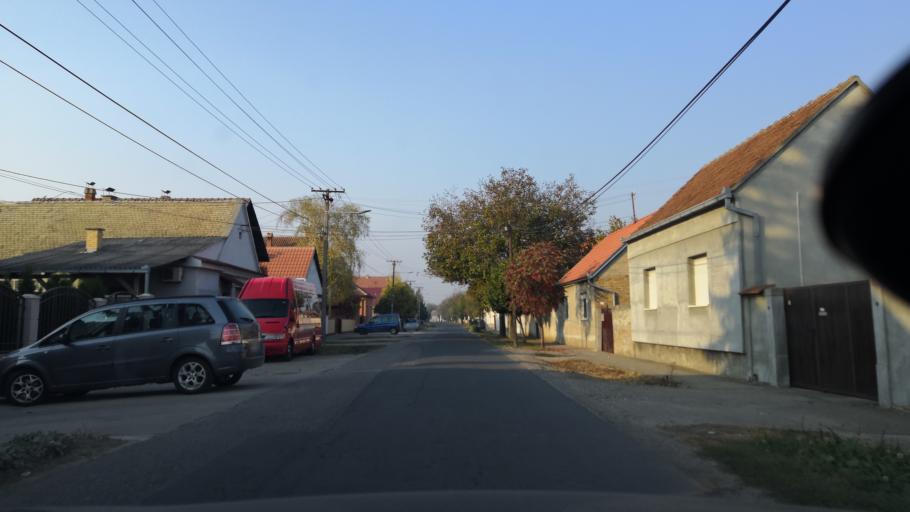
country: RS
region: Autonomna Pokrajina Vojvodina
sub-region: Sremski Okrug
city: Stara Pazova
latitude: 44.9867
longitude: 20.1501
